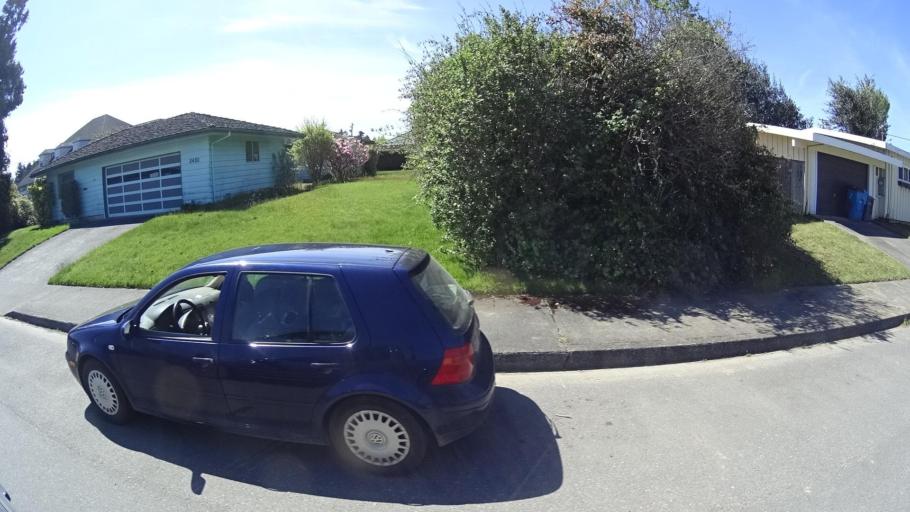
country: US
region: California
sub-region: Humboldt County
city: Myrtletown
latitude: 40.7869
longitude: -124.1409
